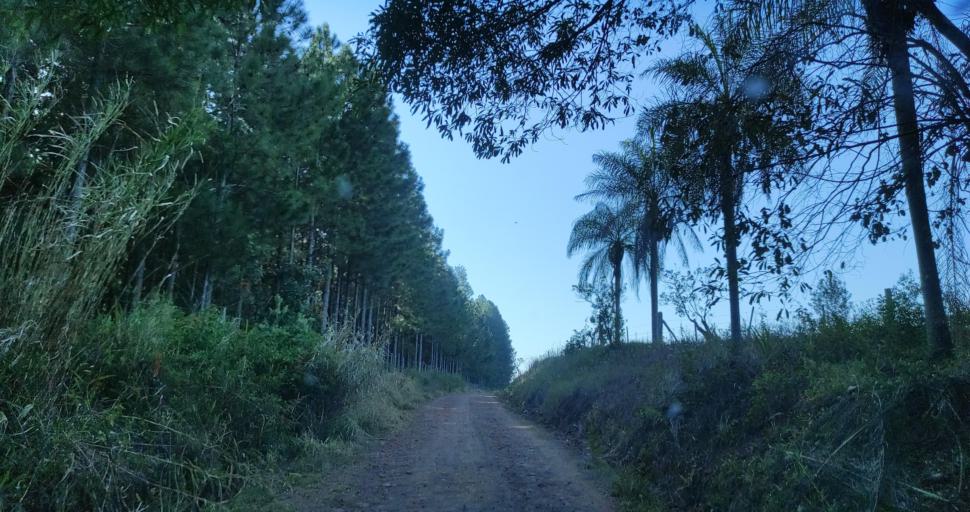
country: AR
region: Misiones
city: Capiovi
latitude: -26.8916
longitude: -55.1073
